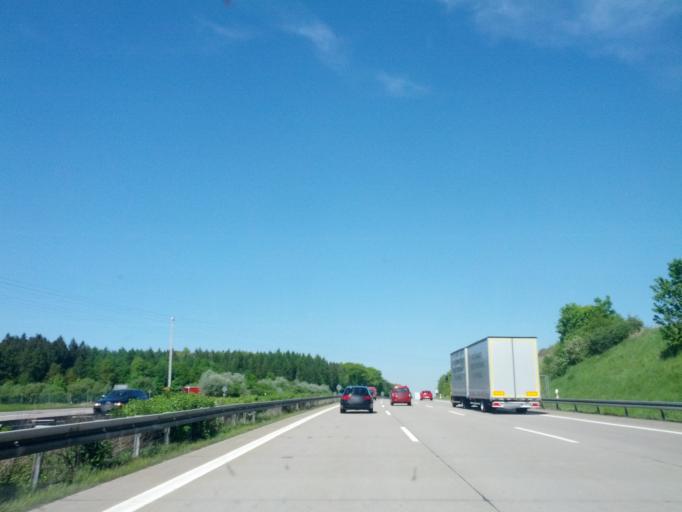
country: DE
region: Saxony
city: Rossau
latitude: 50.9589
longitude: 13.0720
